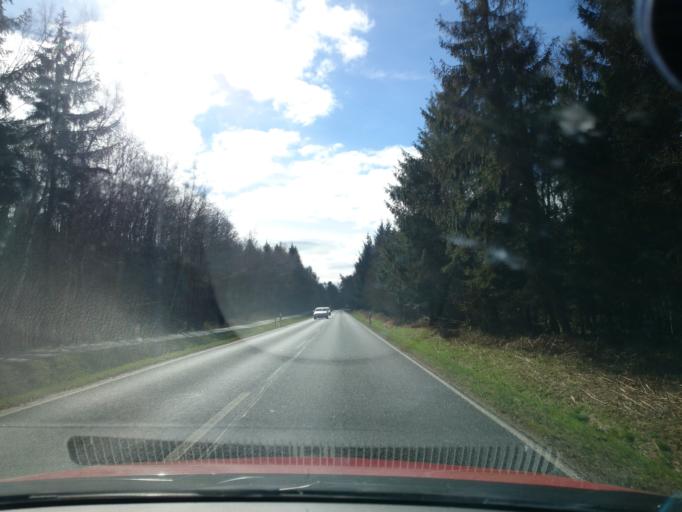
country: DE
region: Mecklenburg-Vorpommern
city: Ostseebad Prerow
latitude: 54.4269
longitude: 12.5729
